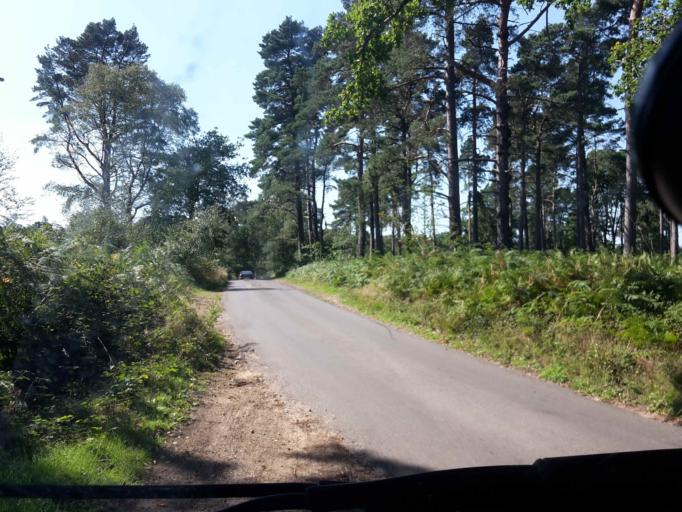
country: GB
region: England
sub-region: Surrey
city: Cranleigh
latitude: 51.1772
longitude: -0.4848
